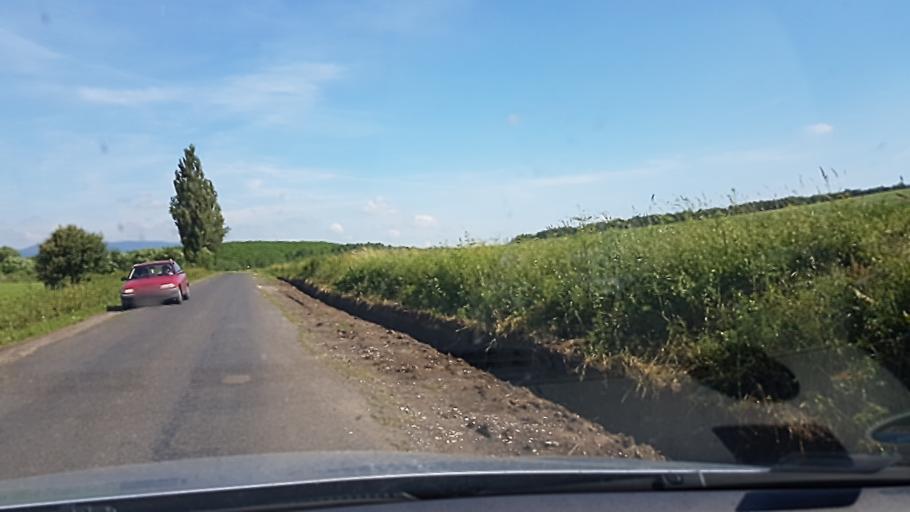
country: HU
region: Borsod-Abauj-Zemplen
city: Saly
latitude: 47.9374
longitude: 20.7101
